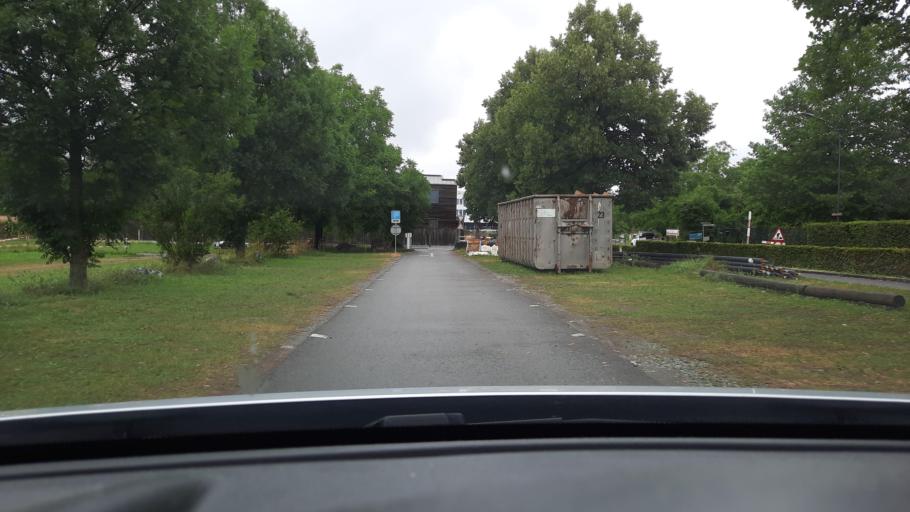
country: LI
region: Schaan
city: Schaan
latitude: 47.1531
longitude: 9.5057
